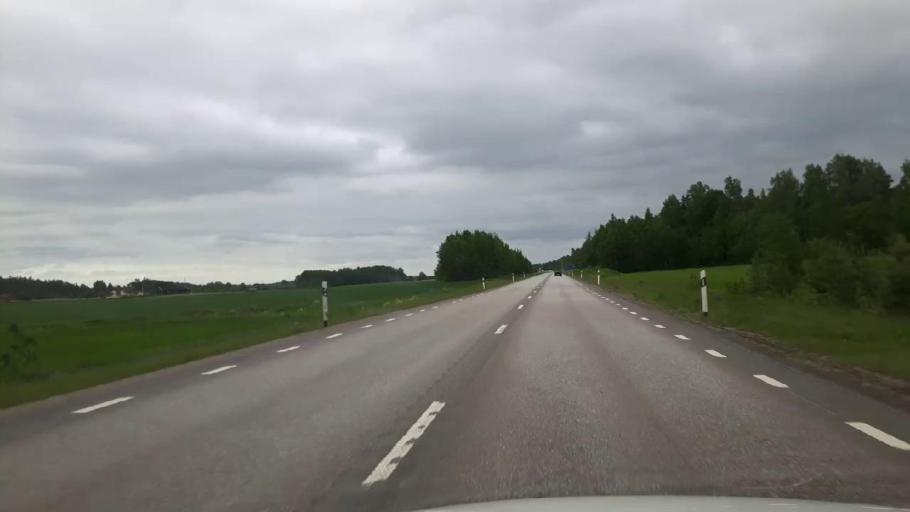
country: SE
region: Vaestmanland
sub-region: Kopings Kommun
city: Koping
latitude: 59.5481
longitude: 15.9207
